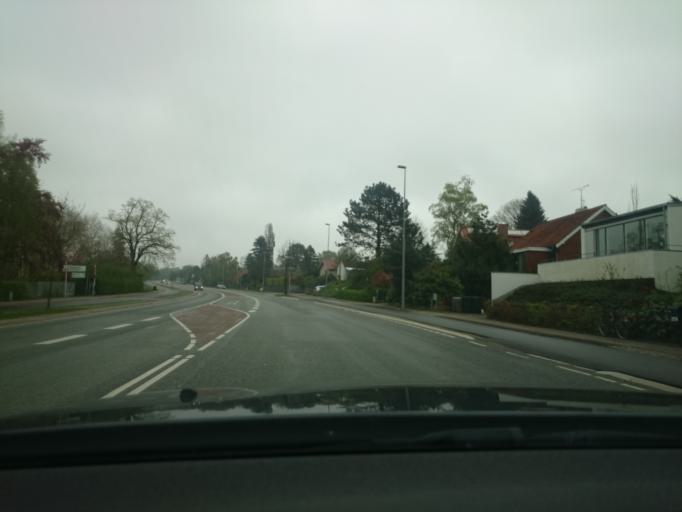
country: DK
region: Capital Region
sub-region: Gladsaxe Municipality
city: Buddinge
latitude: 55.7645
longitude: 12.4570
